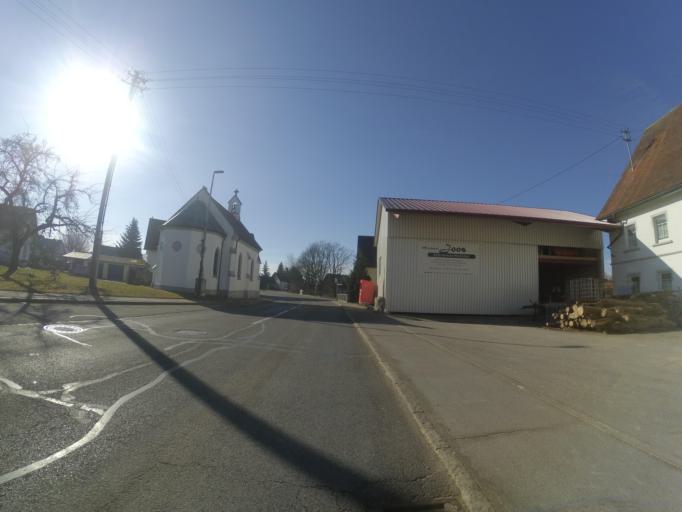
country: DE
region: Baden-Wuerttemberg
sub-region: Tuebingen Region
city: Aulendorf
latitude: 47.9300
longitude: 9.6405
